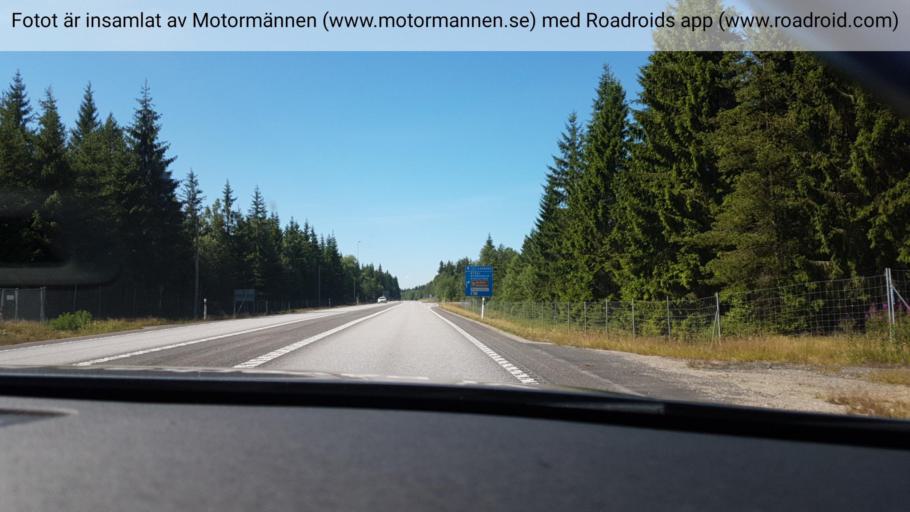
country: SE
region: Vaestra Goetaland
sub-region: Boras Kommun
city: Viskafors
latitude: 57.6302
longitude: 12.8944
